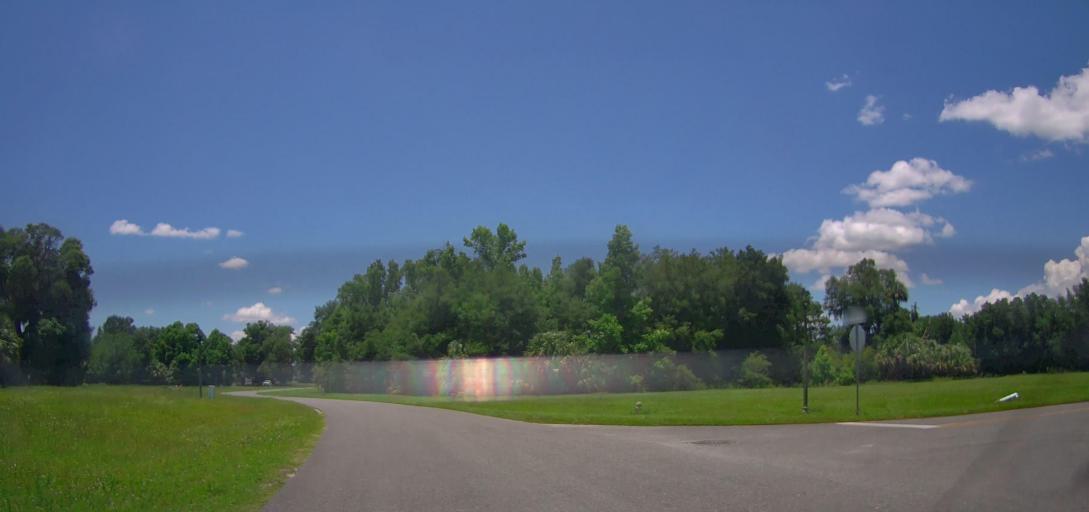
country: US
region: Florida
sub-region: Marion County
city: Belleview
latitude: 29.0912
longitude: -82.0718
